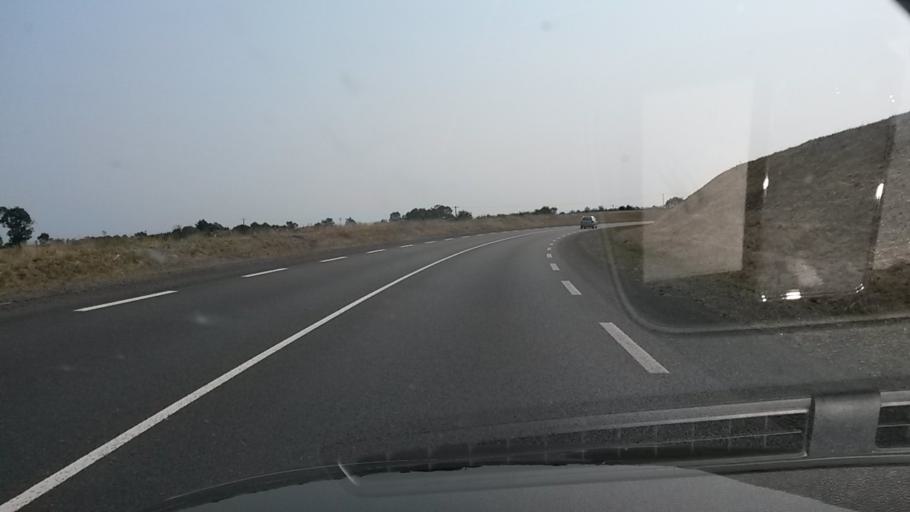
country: FR
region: Pays de la Loire
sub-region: Departement de la Loire-Atlantique
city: Mesanger
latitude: 47.4201
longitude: -1.1849
